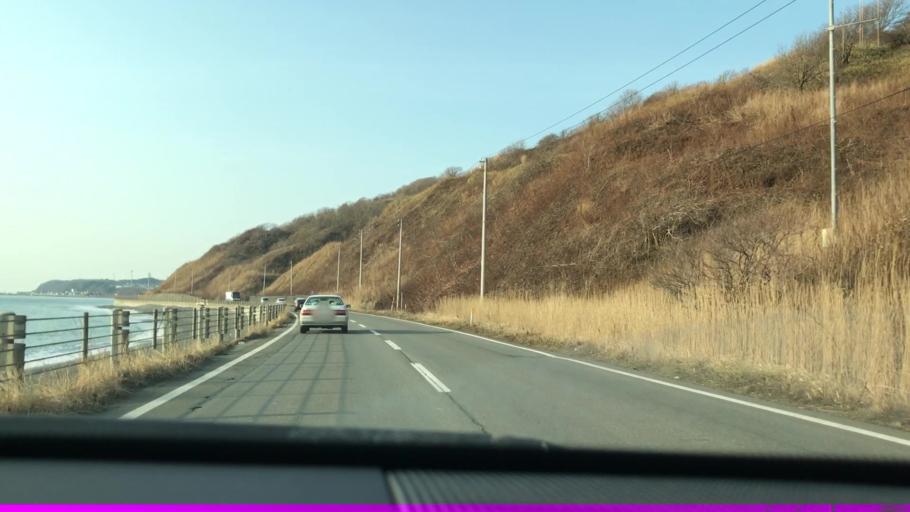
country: JP
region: Hokkaido
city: Shizunai-furukawacho
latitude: 42.2353
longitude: 142.5998
